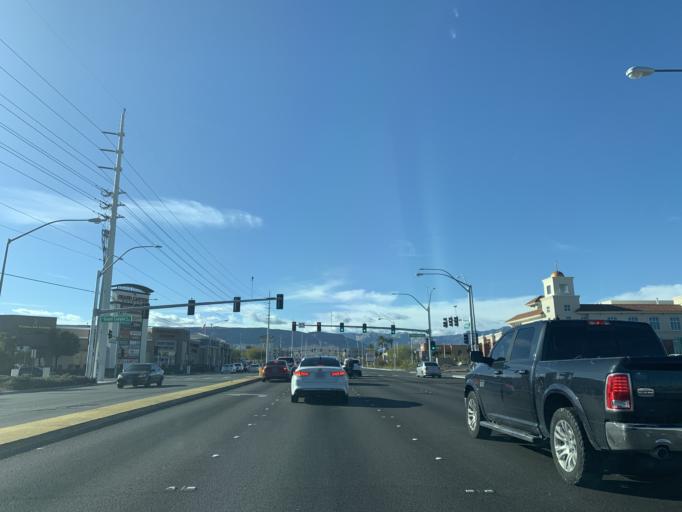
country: US
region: Nevada
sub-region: Clark County
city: Summerlin South
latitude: 36.1152
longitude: -115.3063
